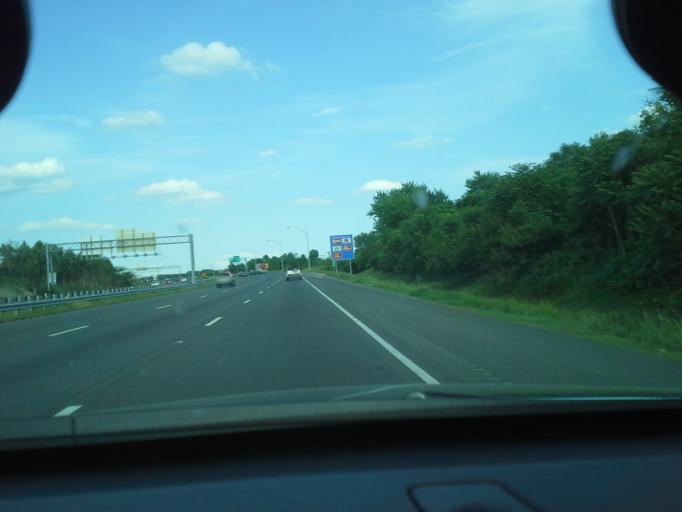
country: US
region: Maryland
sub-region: Frederick County
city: Bartonsville
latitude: 39.4041
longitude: -77.3835
